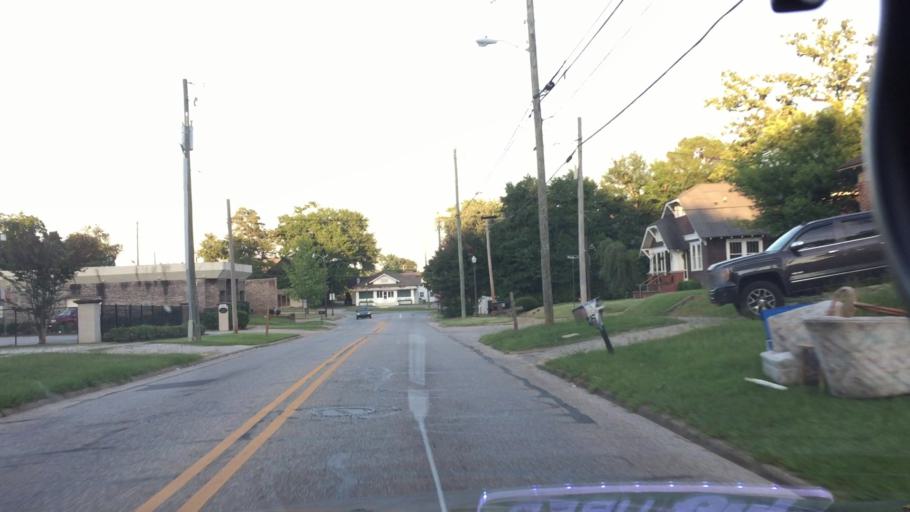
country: US
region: Alabama
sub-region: Lee County
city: Auburn
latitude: 32.6109
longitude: -85.4833
